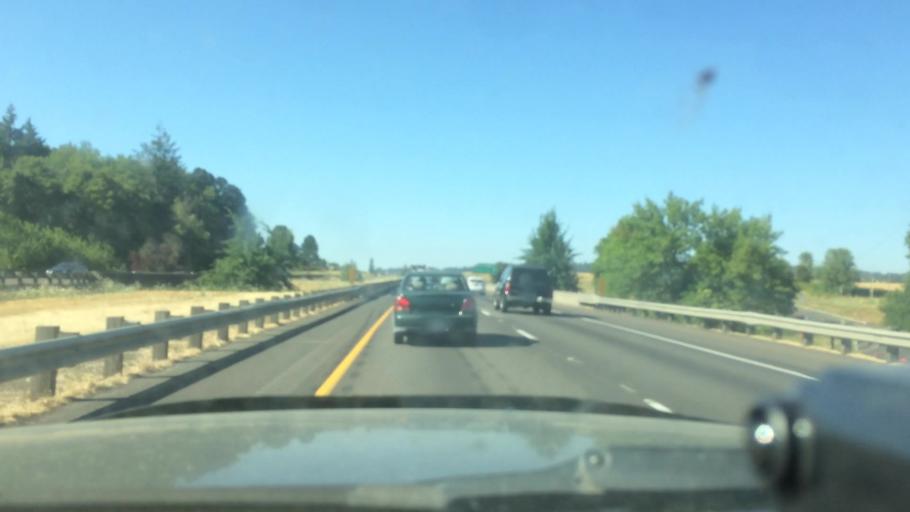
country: US
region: Oregon
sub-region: Linn County
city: Millersburg
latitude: 44.6648
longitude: -123.0590
